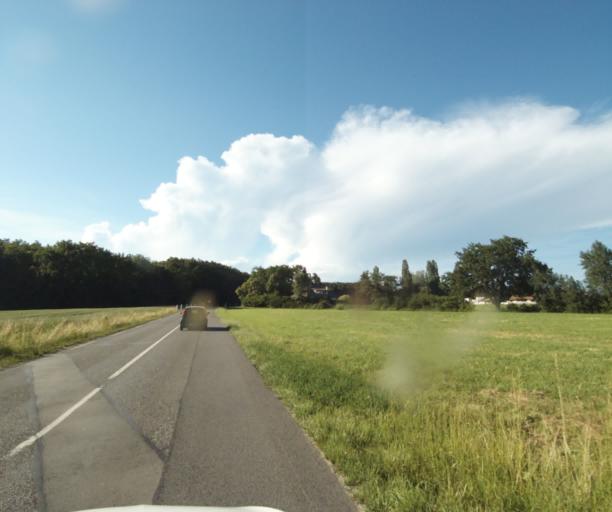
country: FR
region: Rhone-Alpes
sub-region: Departement de la Haute-Savoie
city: Douvaine
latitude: 46.3247
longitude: 6.2931
